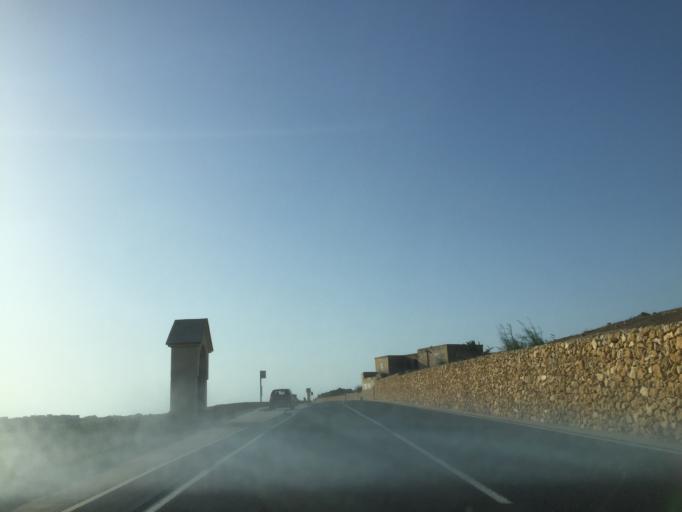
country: MT
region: L-Gharb
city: Gharb
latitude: 36.0550
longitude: 14.2178
